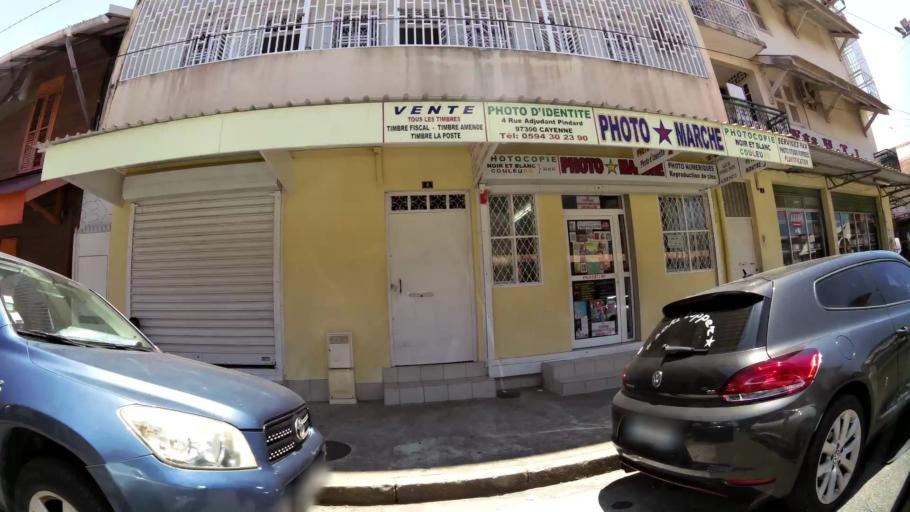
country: GF
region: Guyane
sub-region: Guyane
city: Cayenne
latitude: 4.9357
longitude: -52.3345
